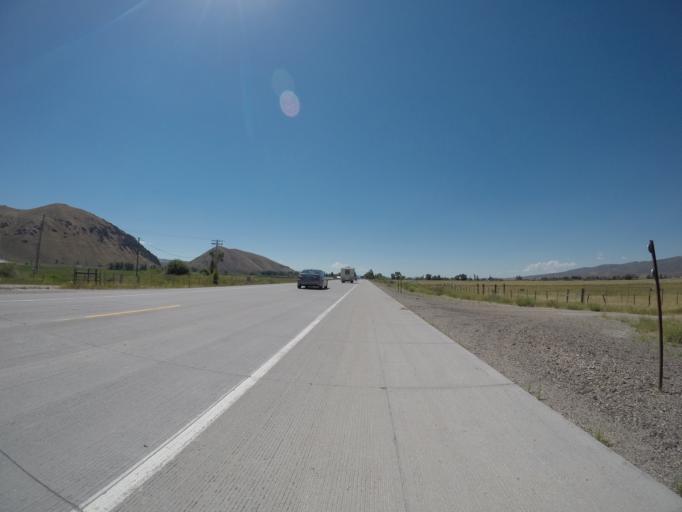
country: US
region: Idaho
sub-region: Bear Lake County
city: Montpelier
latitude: 42.1040
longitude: -110.9541
